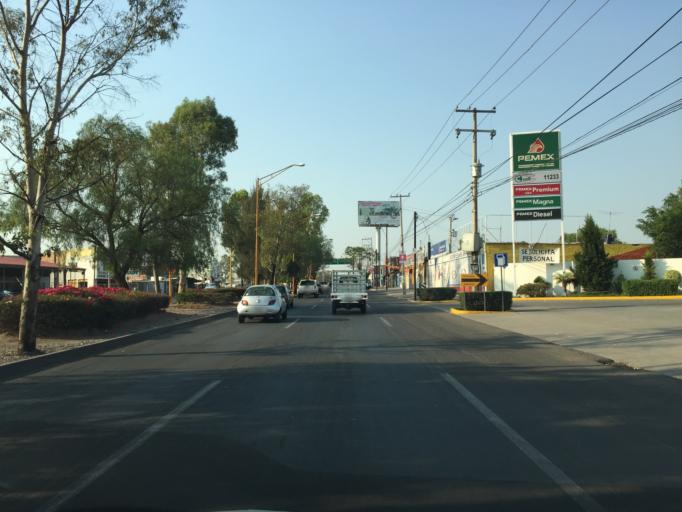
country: MX
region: Aguascalientes
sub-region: Aguascalientes
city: La Loma de los Negritos
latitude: 21.8626
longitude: -102.3174
